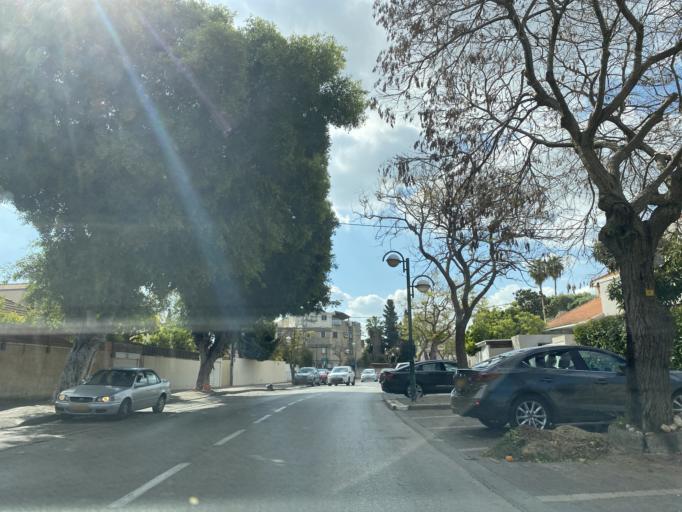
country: IL
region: Tel Aviv
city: Ramat HaSharon
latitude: 32.1339
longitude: 34.8464
